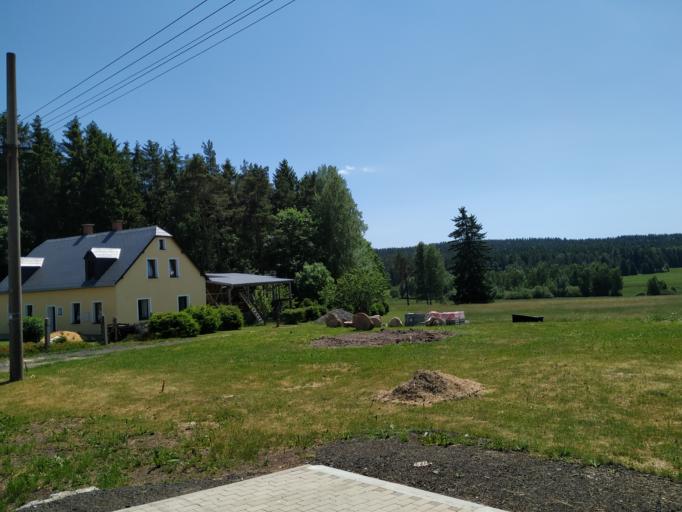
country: CZ
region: Karlovarsky
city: Hranice
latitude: 50.2946
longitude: 12.1896
